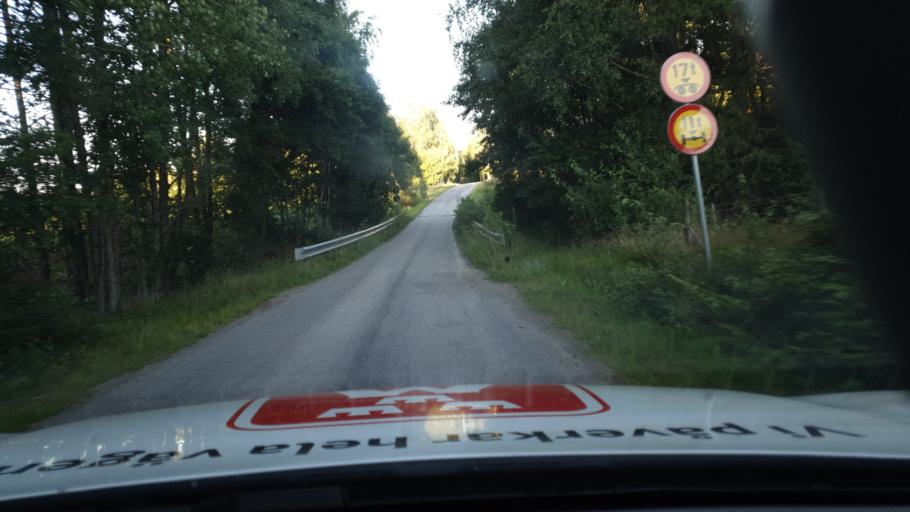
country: SE
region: Vaestra Goetaland
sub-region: Tibro Kommun
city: Tibro
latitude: 58.4323
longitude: 14.0792
